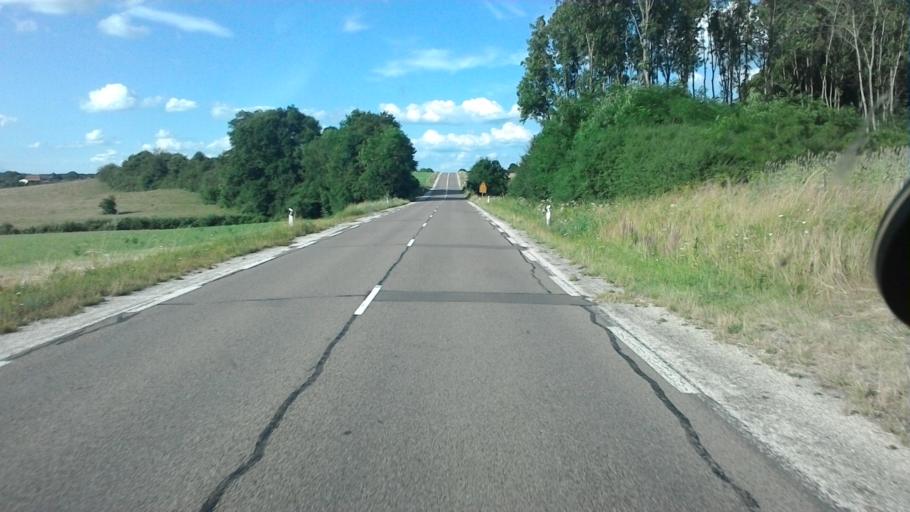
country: FR
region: Franche-Comte
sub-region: Departement de la Haute-Saone
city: Luxeuil-les-Bains
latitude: 47.7129
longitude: 6.2985
